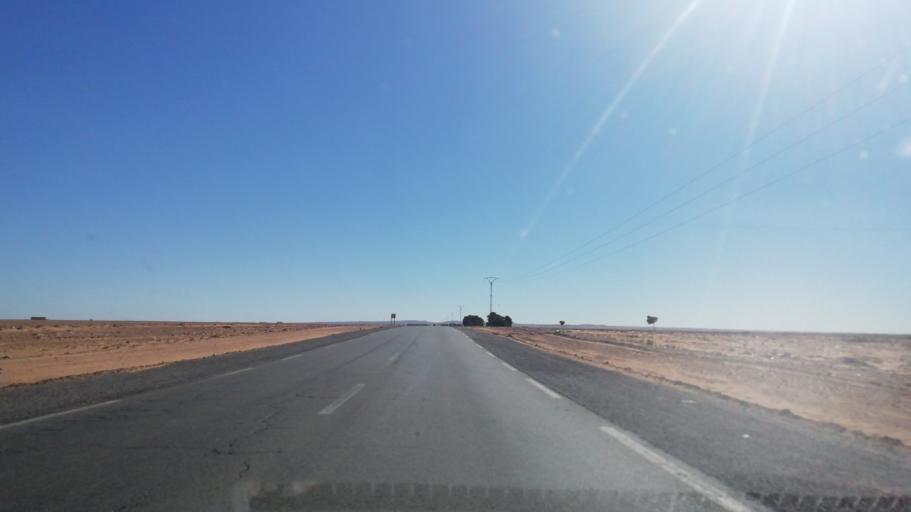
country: DZ
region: Saida
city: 'Ain el Hadjar
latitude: 34.0110
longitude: 0.1172
